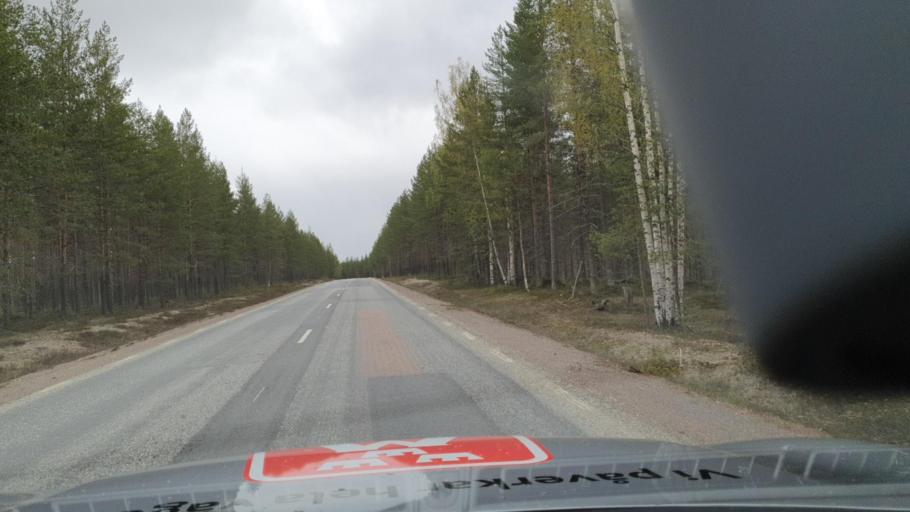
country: SE
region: Vaesternorrland
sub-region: Solleftea Kommun
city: Solleftea
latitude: 63.6442
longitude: 17.3953
